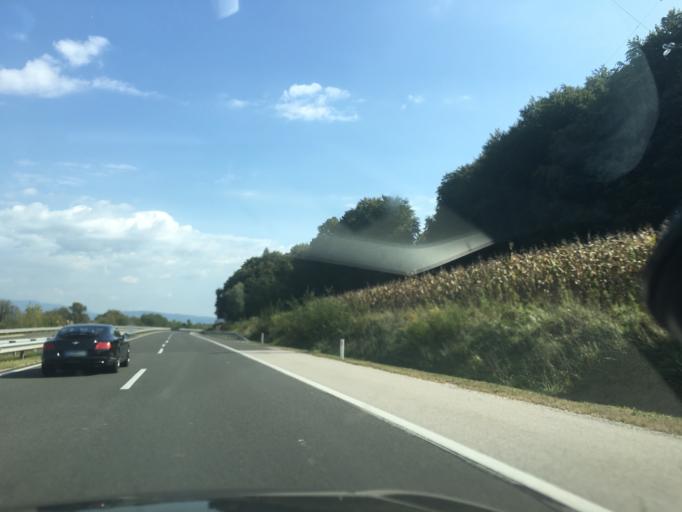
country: HR
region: Zagrebacka
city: Bregana
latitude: 45.8761
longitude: 15.6429
